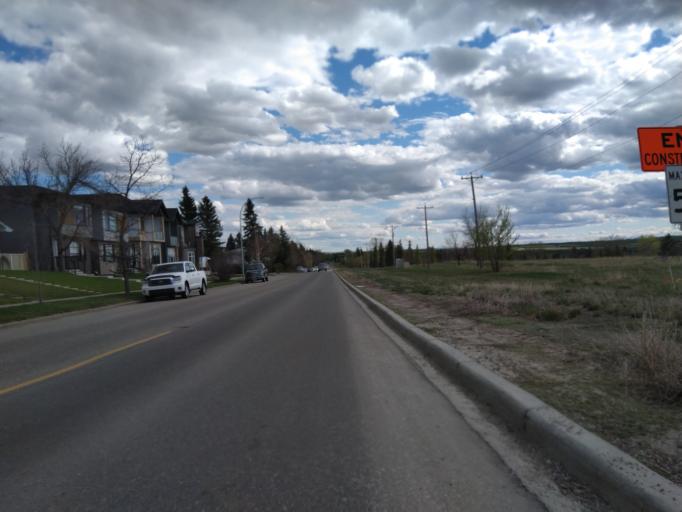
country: CA
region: Alberta
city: Calgary
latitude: 51.0019
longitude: -114.1411
